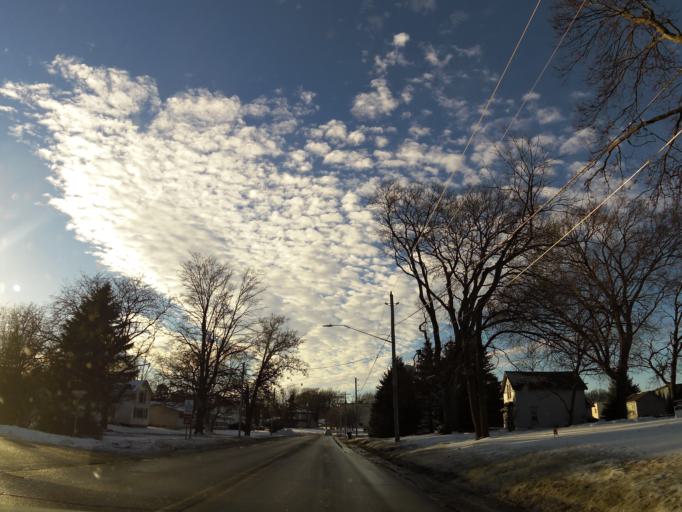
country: US
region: Iowa
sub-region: Butler County
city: Shell Rock
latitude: 42.7149
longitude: -92.5759
